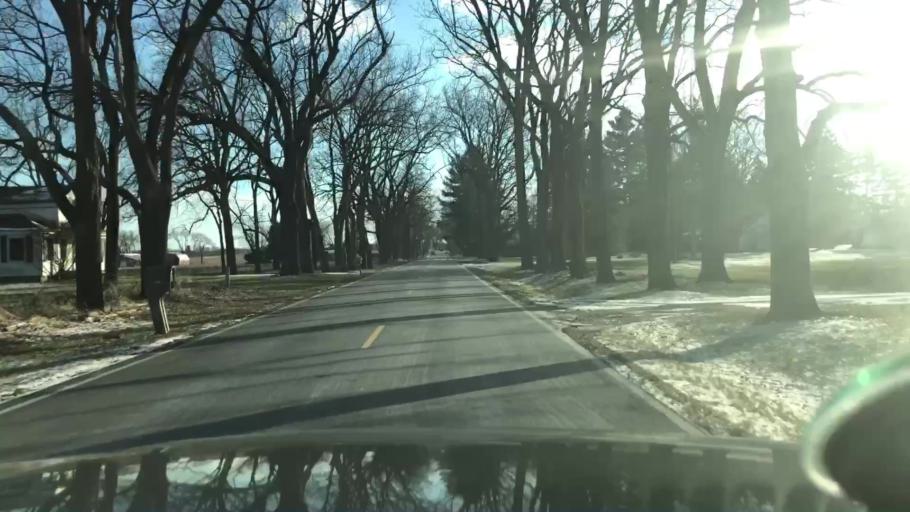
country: US
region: Michigan
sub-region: Jackson County
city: Vandercook Lake
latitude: 42.1733
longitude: -84.4521
